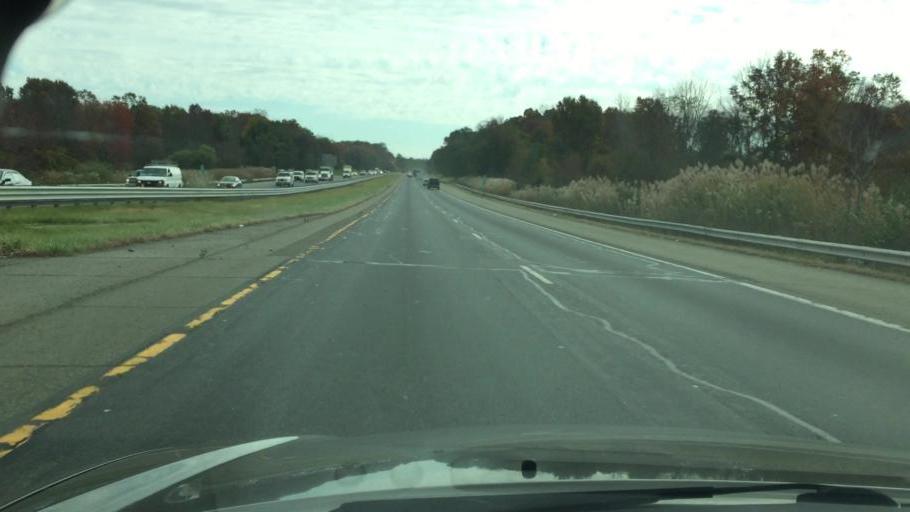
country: US
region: New Jersey
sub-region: Morris County
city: Madison
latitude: 40.7817
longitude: -74.4147
